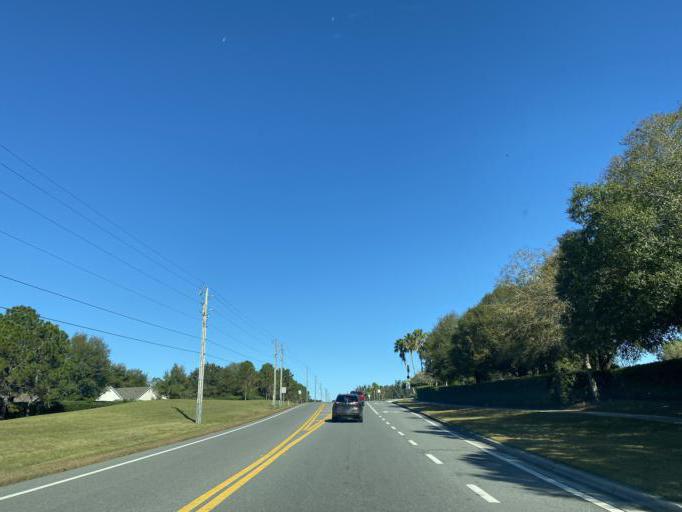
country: US
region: Florida
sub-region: Lake County
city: Minneola
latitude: 28.5118
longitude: -81.7070
